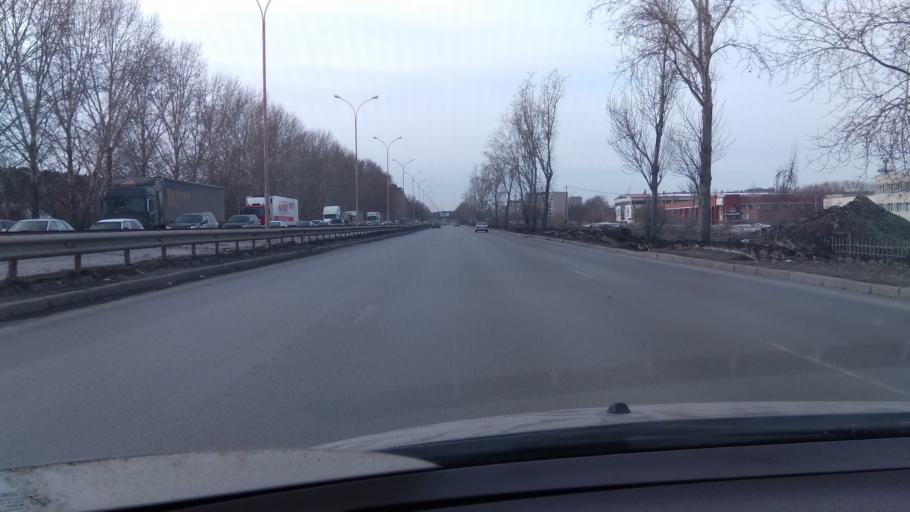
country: RU
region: Sverdlovsk
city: Sovkhoznyy
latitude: 56.7946
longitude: 60.5656
